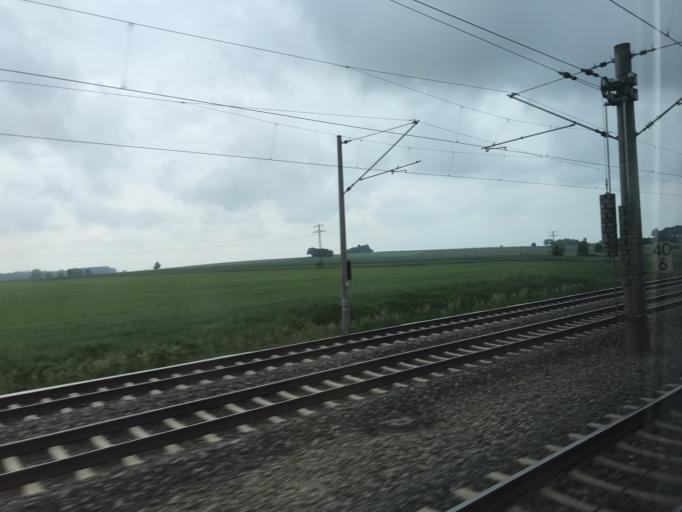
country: DE
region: Bavaria
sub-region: Upper Bavaria
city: Althegnenberg
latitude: 48.2395
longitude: 11.0546
